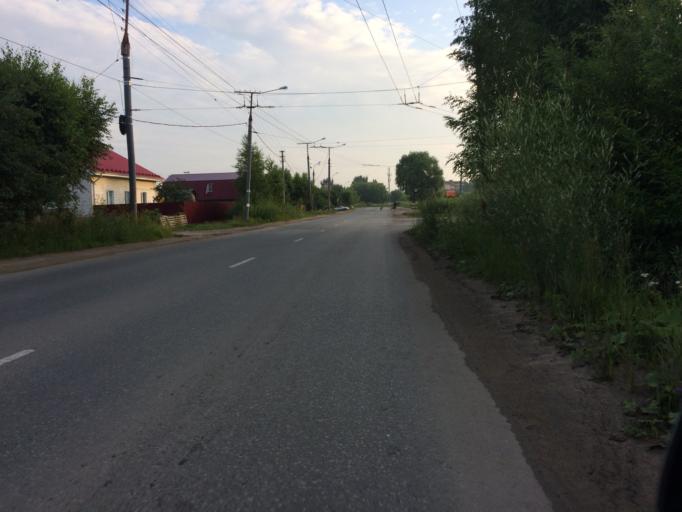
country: RU
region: Mariy-El
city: Yoshkar-Ola
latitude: 56.6454
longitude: 47.9544
